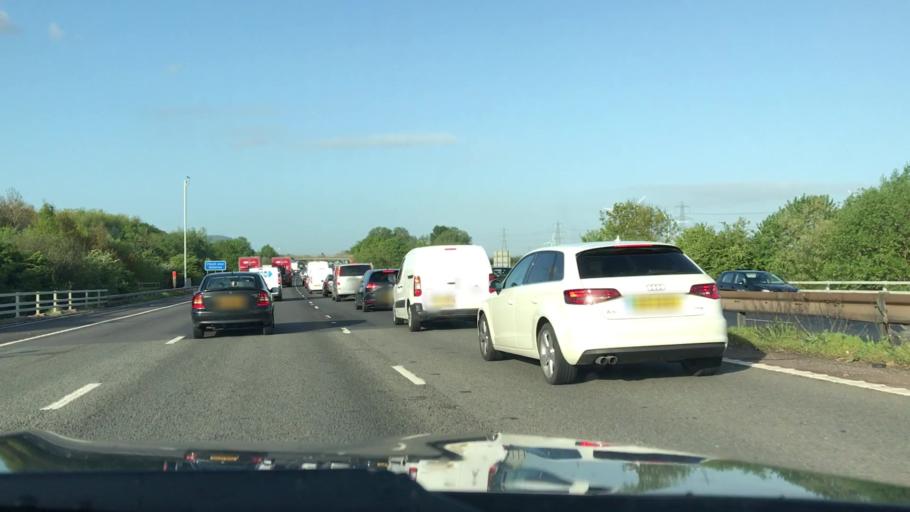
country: GB
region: England
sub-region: Cheshire West and Chester
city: Frodsham
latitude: 53.3050
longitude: -2.7167
